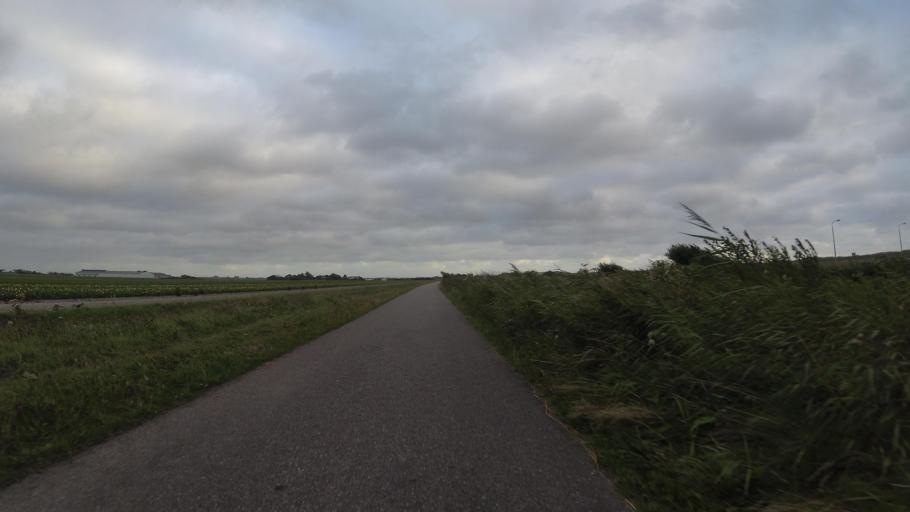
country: NL
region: North Holland
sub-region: Gemeente Den Helder
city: Den Helder
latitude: 52.9210
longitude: 4.7290
